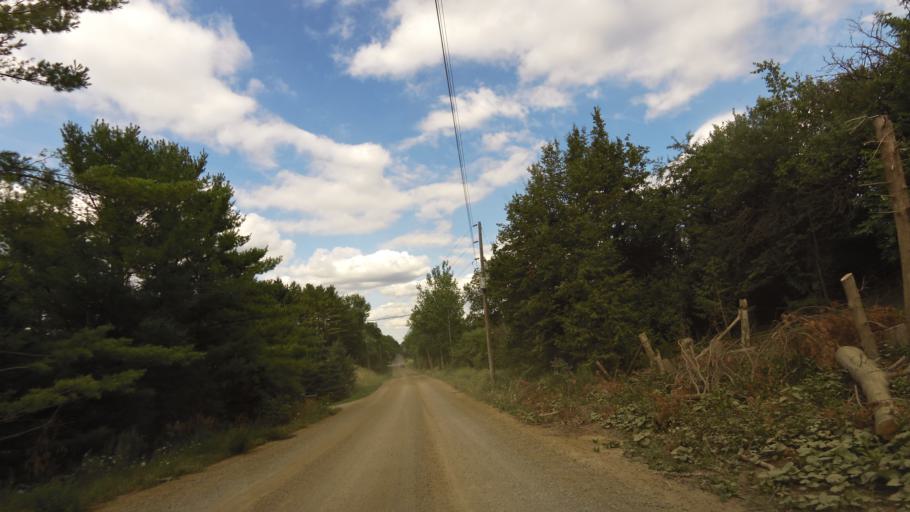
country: CA
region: Ontario
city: Orangeville
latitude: 43.9811
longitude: -79.9455
